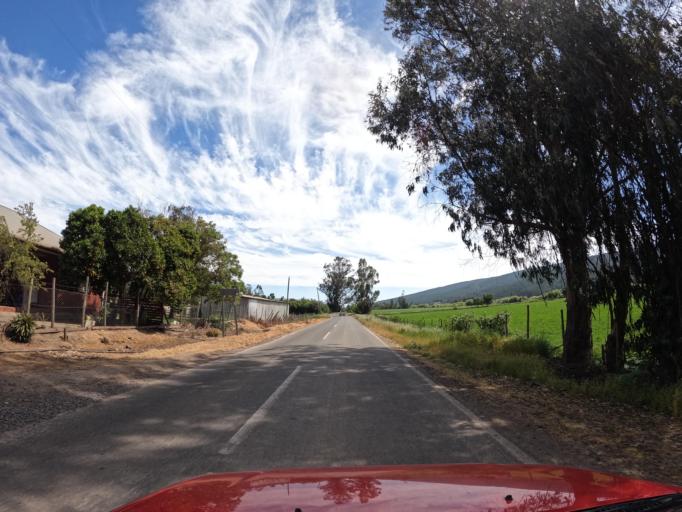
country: CL
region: Maule
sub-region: Provincia de Talca
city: Constitucion
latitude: -35.0062
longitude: -72.0308
